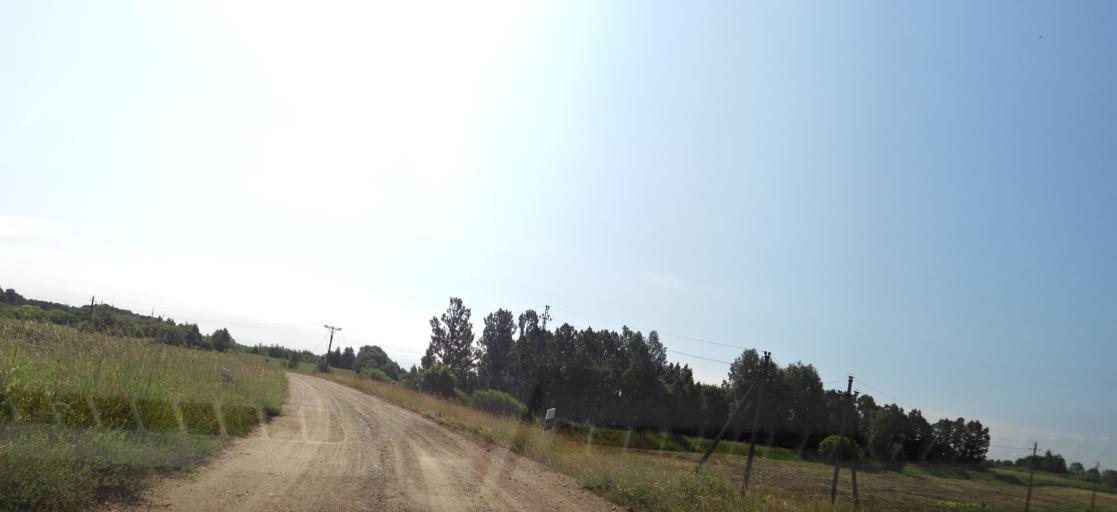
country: LT
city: Grigiskes
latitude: 54.8638
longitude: 25.0619
